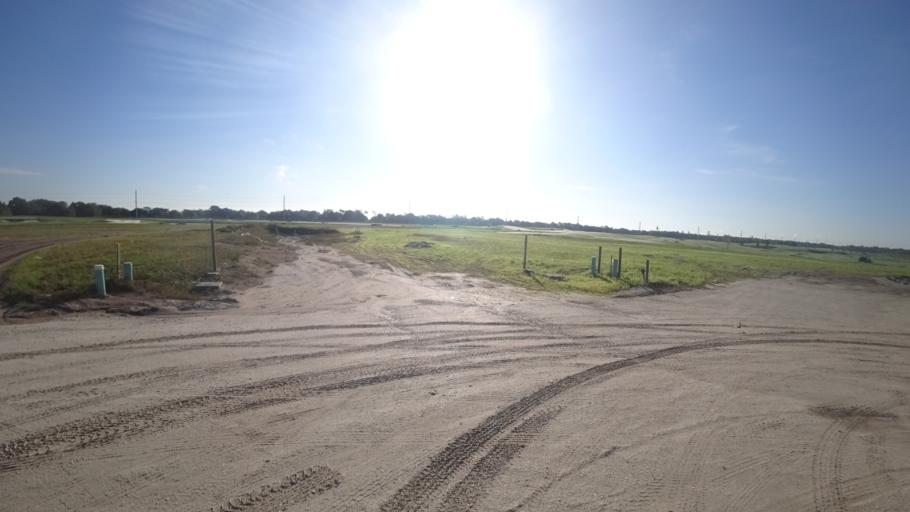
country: US
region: Florida
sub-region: Sarasota County
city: The Meadows
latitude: 27.4421
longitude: -82.3547
